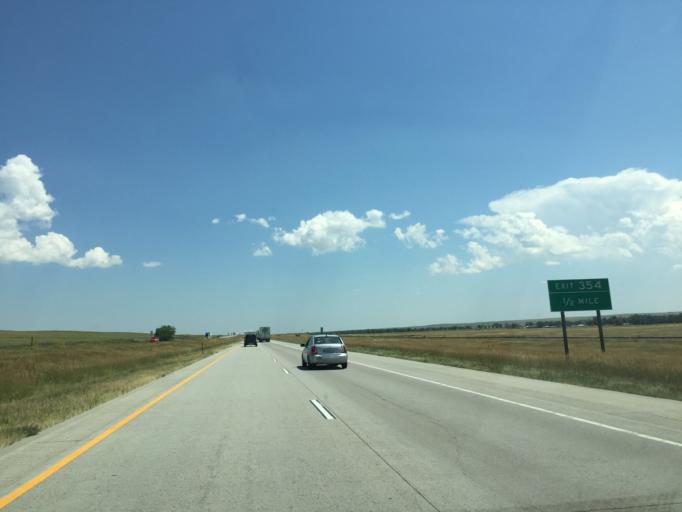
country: US
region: Colorado
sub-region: Lincoln County
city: Limon
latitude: 39.2963
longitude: -103.8043
